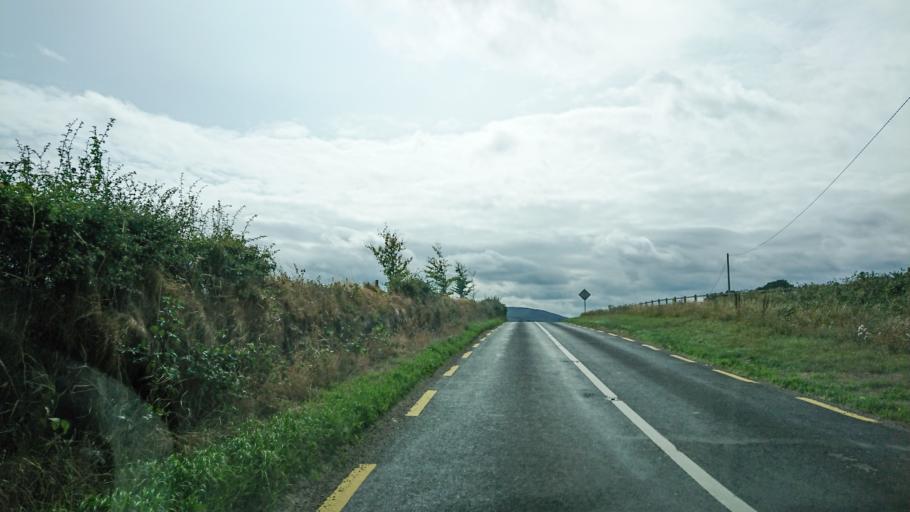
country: IE
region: Munster
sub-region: County Cork
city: Mallow
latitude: 52.1583
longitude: -8.4875
